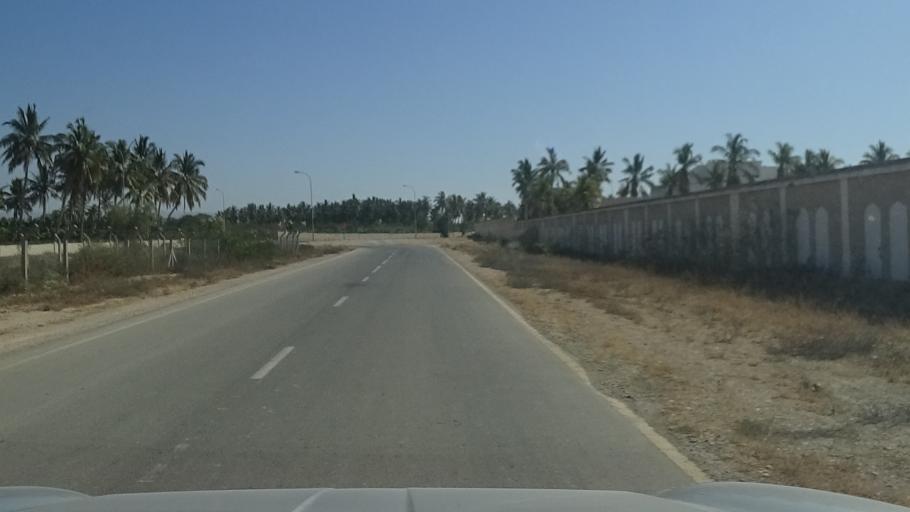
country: OM
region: Zufar
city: Salalah
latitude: 17.0338
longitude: 54.1524
